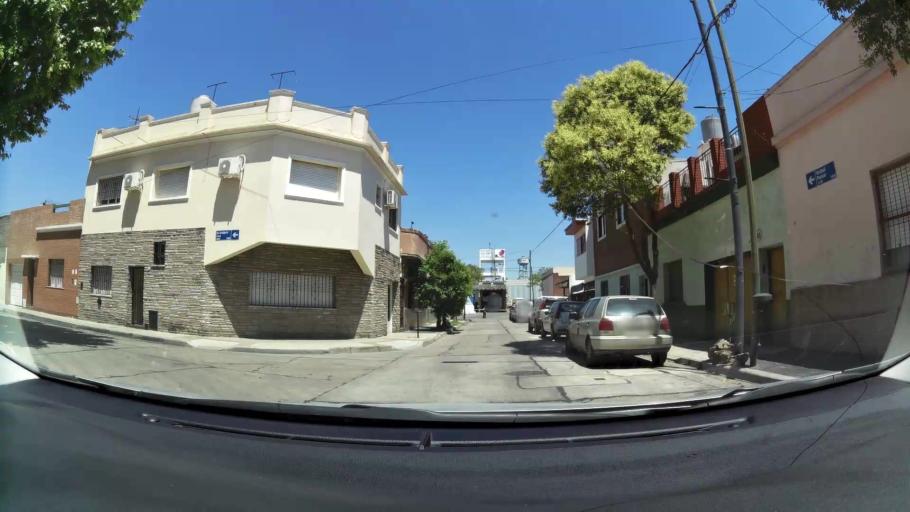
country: AR
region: Buenos Aires
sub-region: Partido de Avellaneda
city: Avellaneda
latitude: -34.6536
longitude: -58.3936
